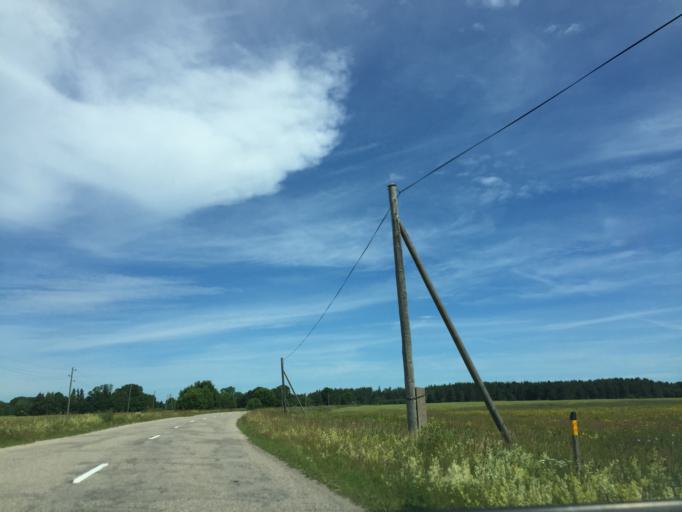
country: LV
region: Dundaga
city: Dundaga
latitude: 57.5307
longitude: 22.3290
